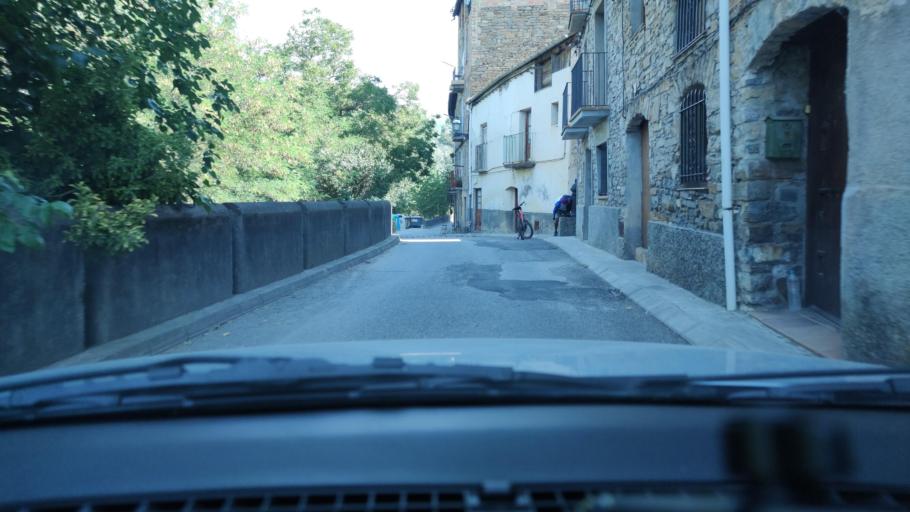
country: ES
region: Catalonia
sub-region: Provincia de Lleida
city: Senterada
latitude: 42.2440
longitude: 0.9713
